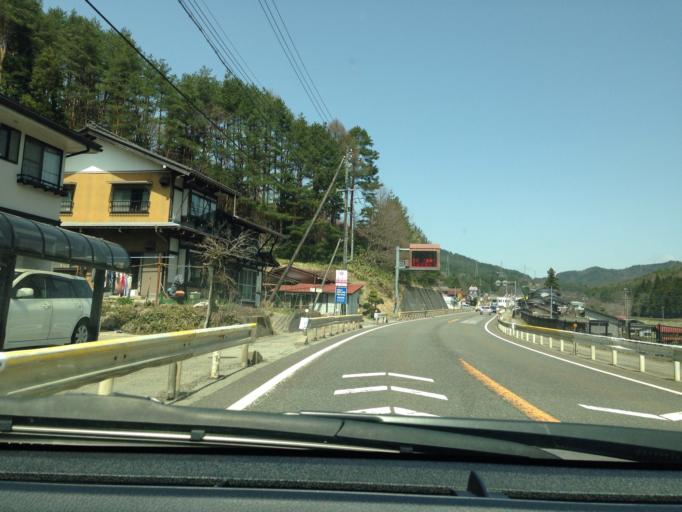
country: JP
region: Gifu
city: Takayama
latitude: 36.0594
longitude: 137.2714
